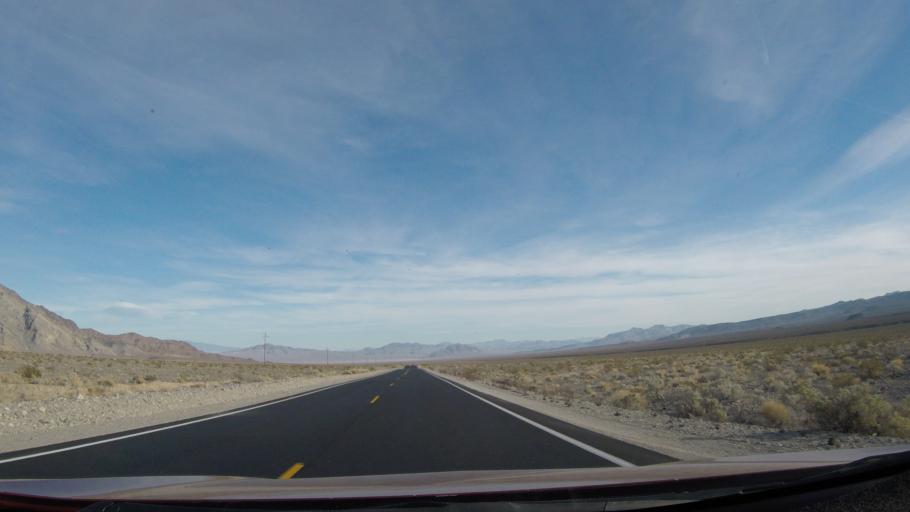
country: US
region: Nevada
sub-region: Nye County
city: Pahrump
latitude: 36.3248
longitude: -116.5624
